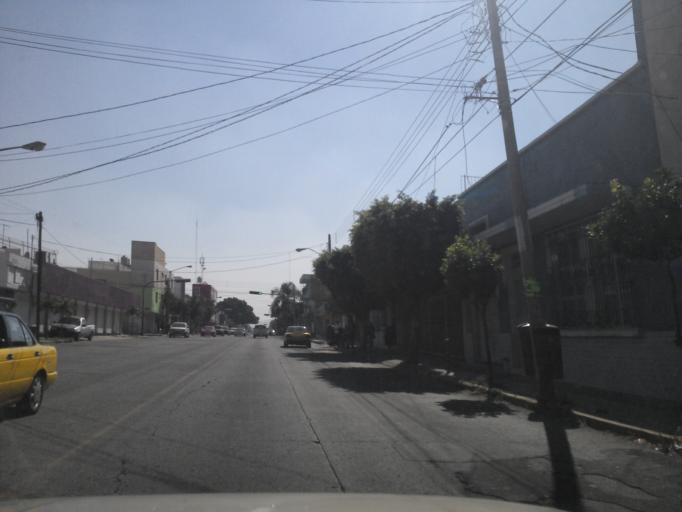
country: MX
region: Jalisco
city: Guadalajara
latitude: 20.6853
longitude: -103.3592
